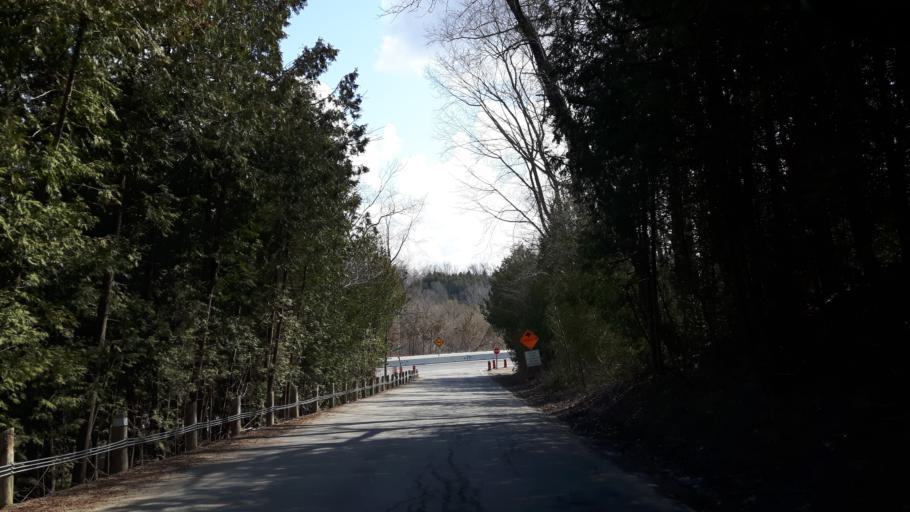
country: CA
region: Ontario
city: Bluewater
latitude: 43.5674
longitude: -81.6983
